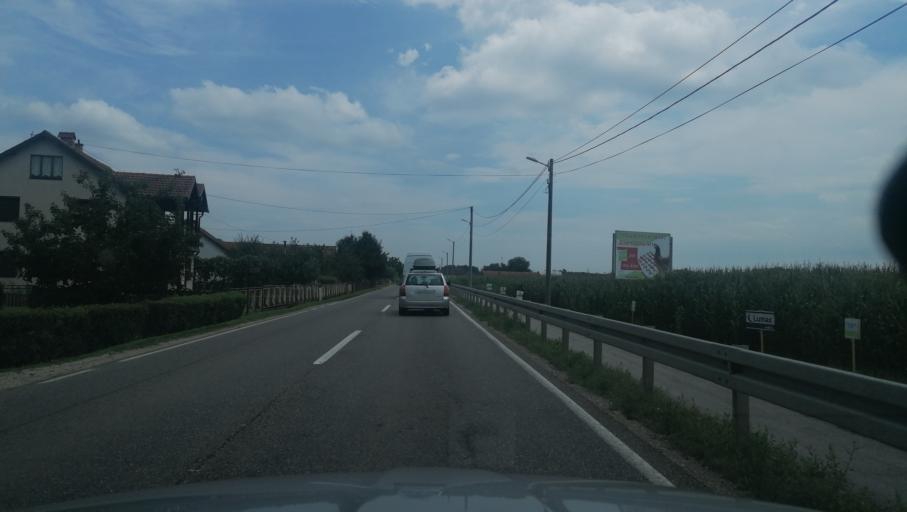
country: BA
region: Republika Srpska
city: Obudovac
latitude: 44.9573
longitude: 18.6323
